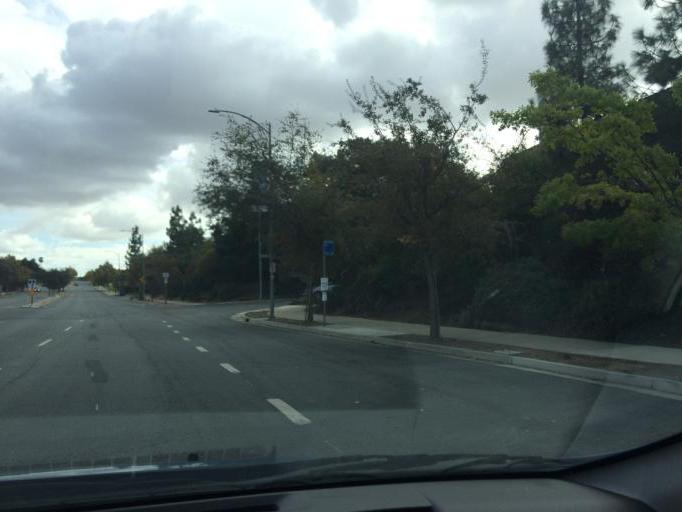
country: US
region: California
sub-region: Santa Clara County
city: Seven Trees
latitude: 37.2967
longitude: -121.7695
